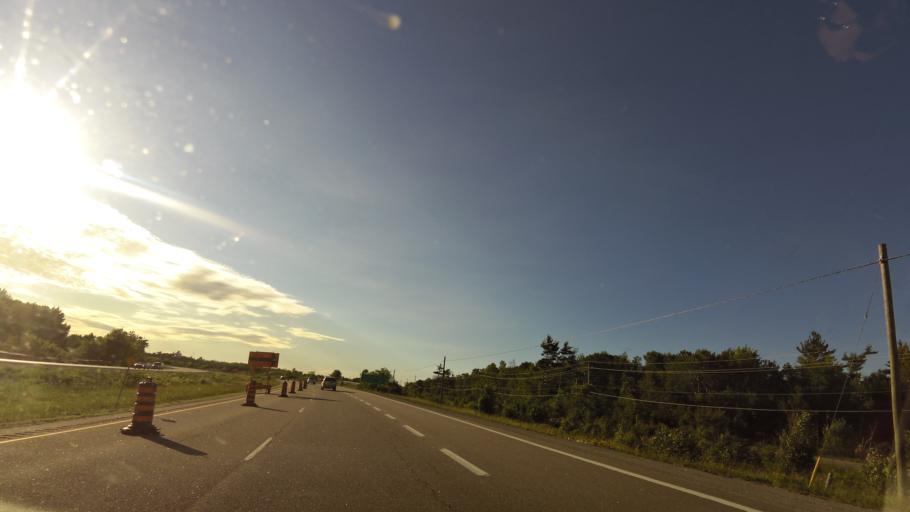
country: CA
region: Ontario
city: Midland
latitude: 44.7950
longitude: -79.7078
